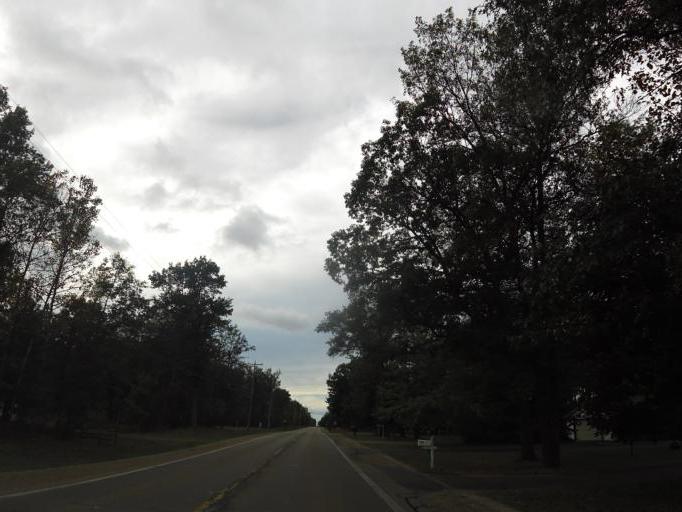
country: US
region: Michigan
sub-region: Roscommon County
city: Saint Helen
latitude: 44.3489
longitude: -84.4490
